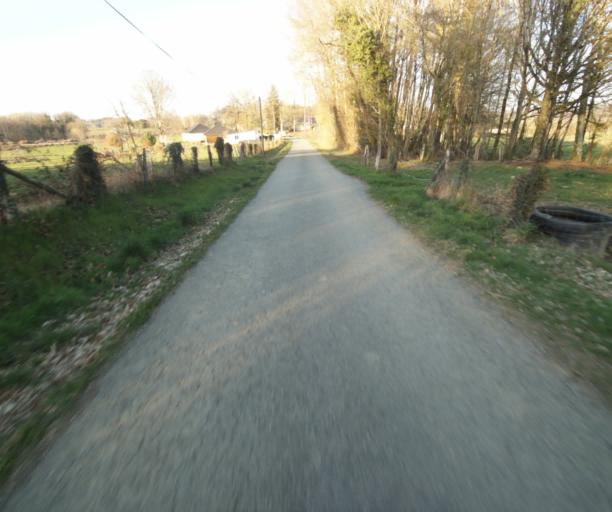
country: FR
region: Limousin
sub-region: Departement de la Correze
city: Uzerche
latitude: 45.3590
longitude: 1.5952
